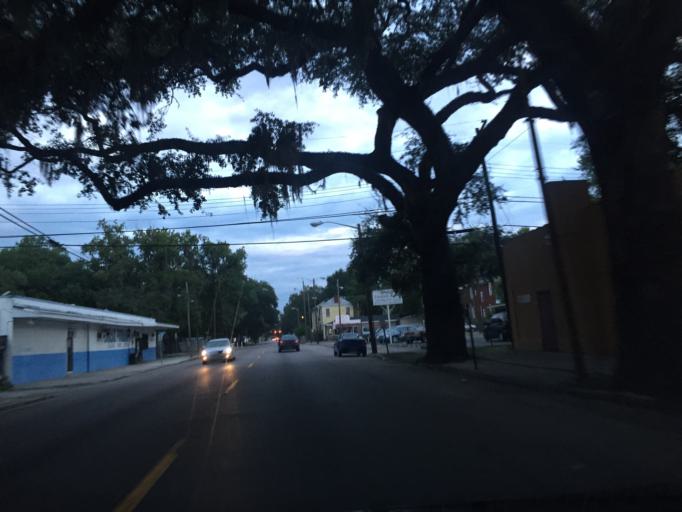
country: US
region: Georgia
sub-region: Chatham County
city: Savannah
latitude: 32.0550
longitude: -81.1055
